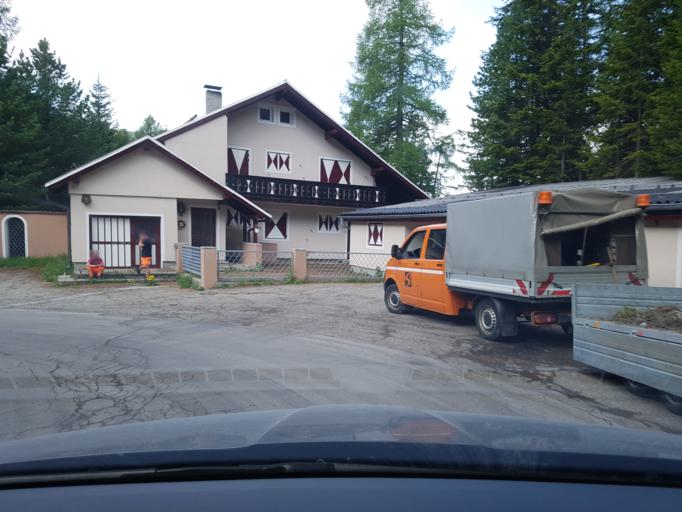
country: AT
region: Salzburg
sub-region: Politischer Bezirk Tamsweg
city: Thomatal
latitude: 46.9715
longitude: 13.7614
